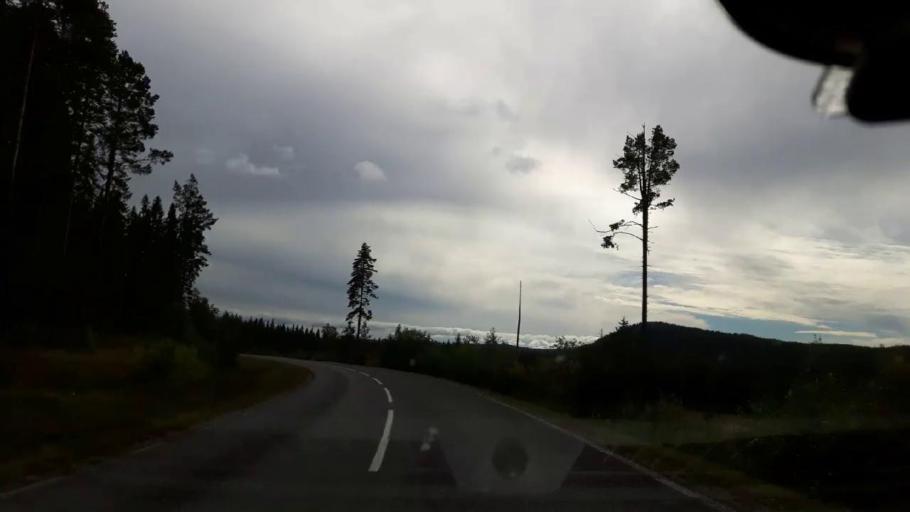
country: SE
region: Jaemtland
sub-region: Ragunda Kommun
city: Hammarstrand
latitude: 63.0694
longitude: 15.9174
